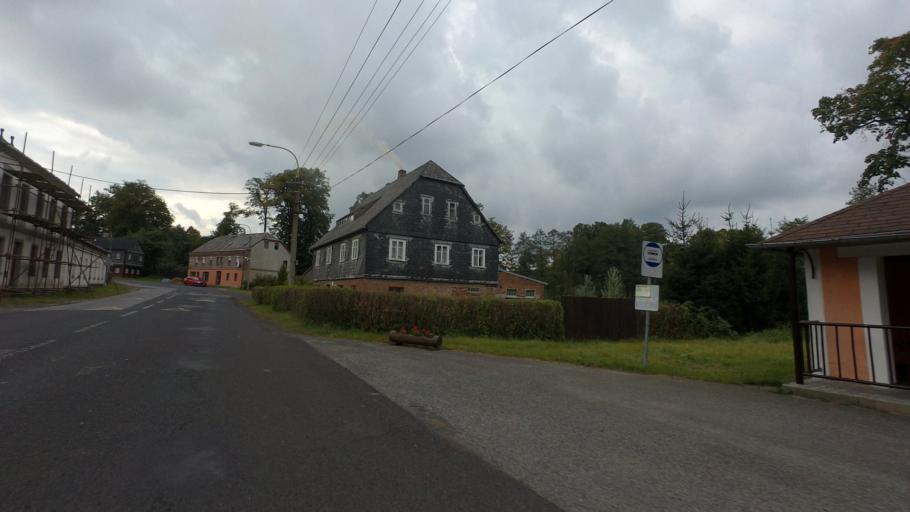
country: CZ
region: Ustecky
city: Velky Senov
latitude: 51.0113
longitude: 14.3584
